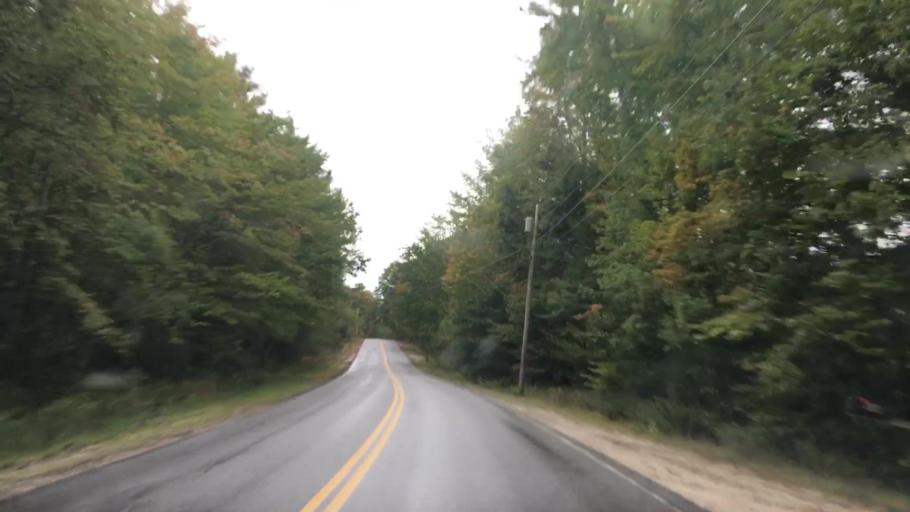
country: US
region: Maine
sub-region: Cumberland County
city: Raymond
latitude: 43.9364
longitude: -70.4231
